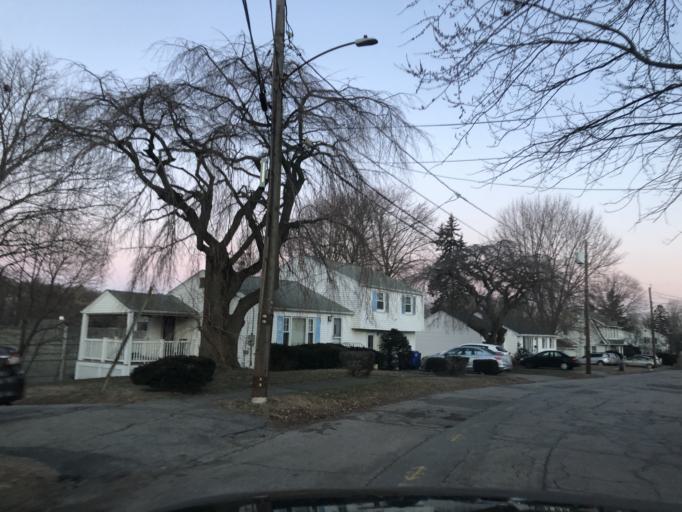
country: US
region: Massachusetts
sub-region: Norfolk County
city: Milton
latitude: 42.2640
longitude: -71.0445
